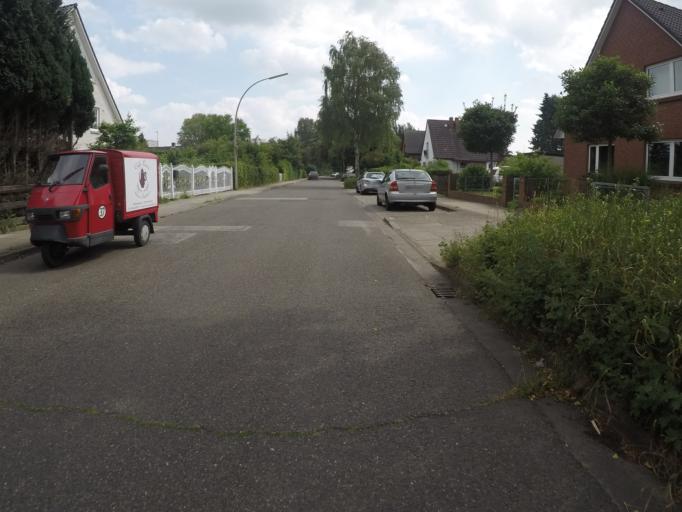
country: DE
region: Hamburg
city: Wandsbek
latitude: 53.5489
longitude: 10.1167
